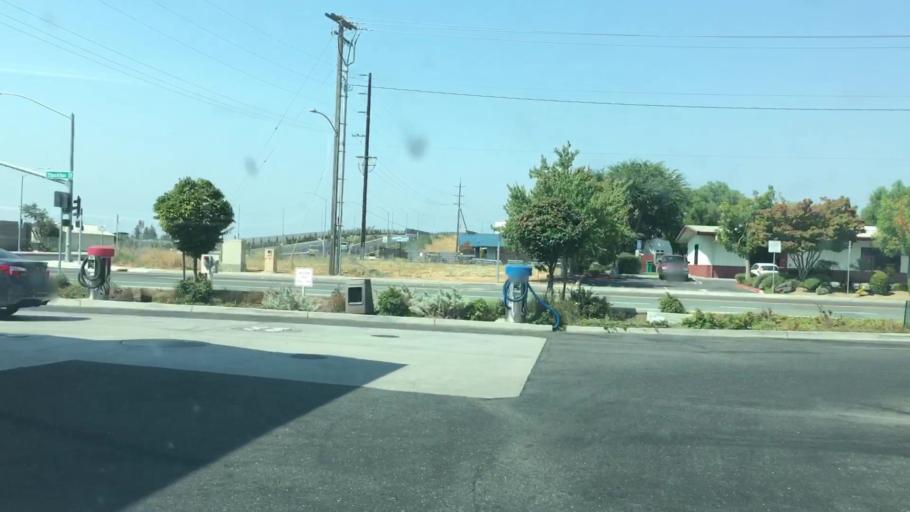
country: US
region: California
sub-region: San Joaquin County
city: Lodi
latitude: 38.1017
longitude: -121.2691
